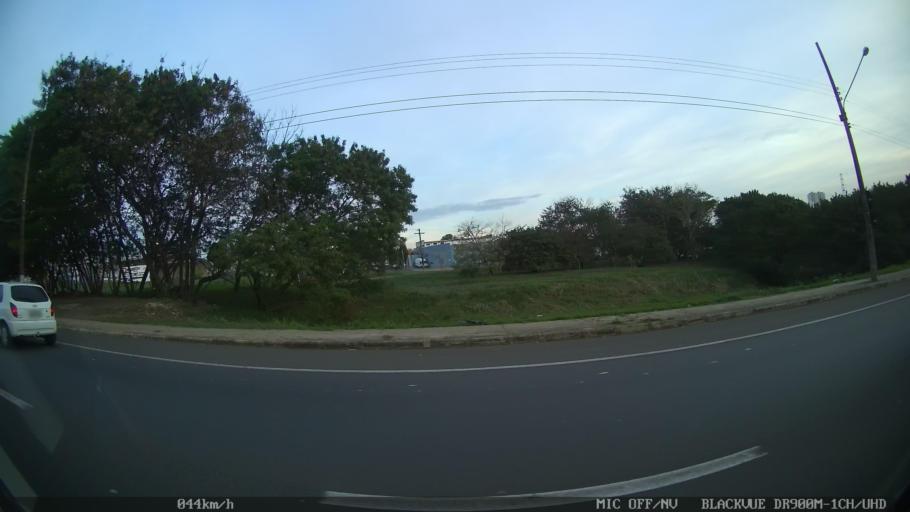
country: BR
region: Sao Paulo
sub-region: Limeira
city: Limeira
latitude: -22.5437
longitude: -47.4036
